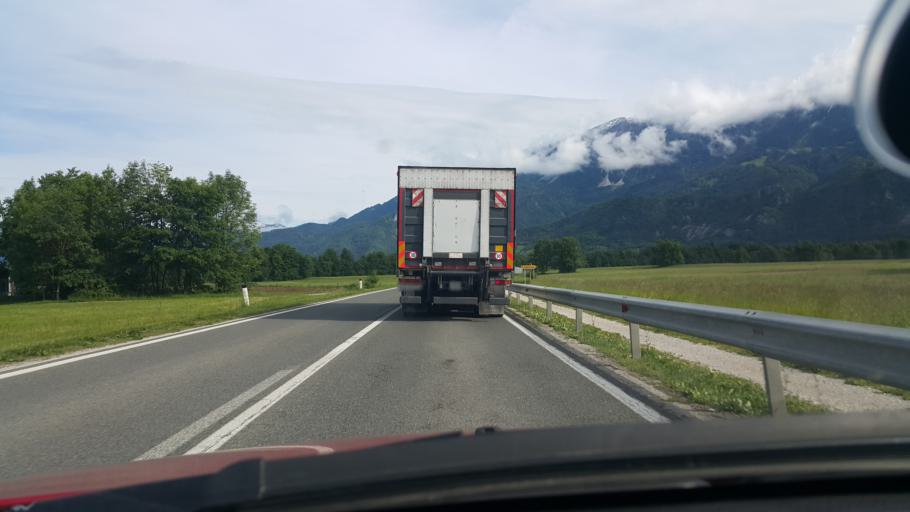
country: SI
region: Radovljica
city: Lesce
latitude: 46.3726
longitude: 14.1509
